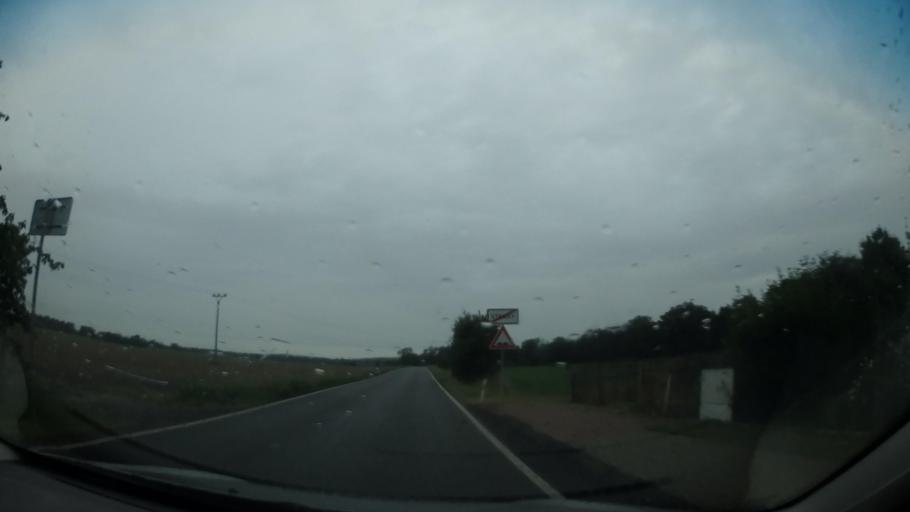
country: CZ
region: Central Bohemia
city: Milovice
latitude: 50.2399
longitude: 14.9522
